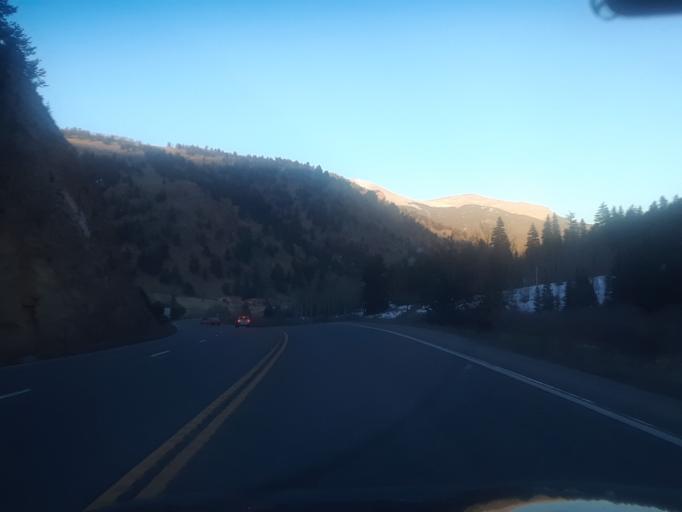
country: US
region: Colorado
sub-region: Clear Creek County
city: Georgetown
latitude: 39.4523
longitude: -105.7291
